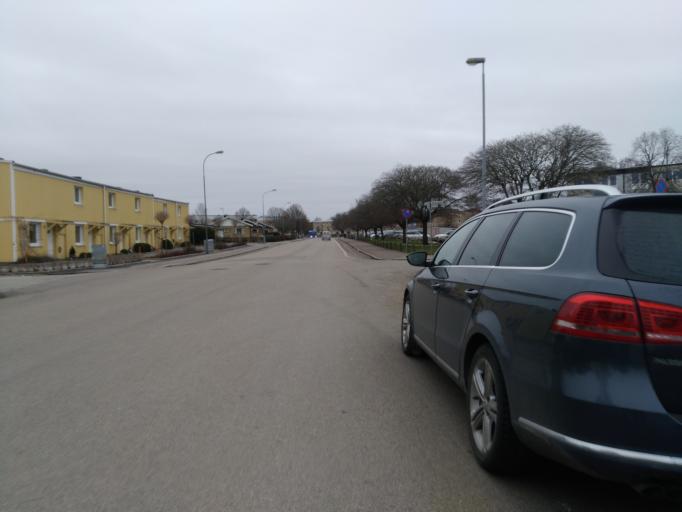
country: SE
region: Vaestra Goetaland
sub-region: Lidkopings Kommun
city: Lidkoping
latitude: 58.4954
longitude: 13.1584
